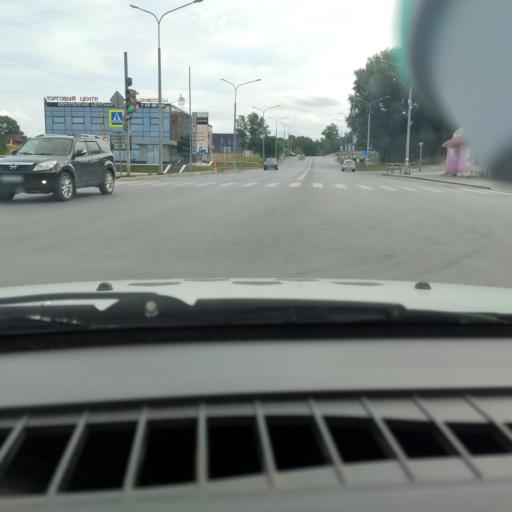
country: RU
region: Perm
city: Solikamsk
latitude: 59.6483
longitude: 56.7710
